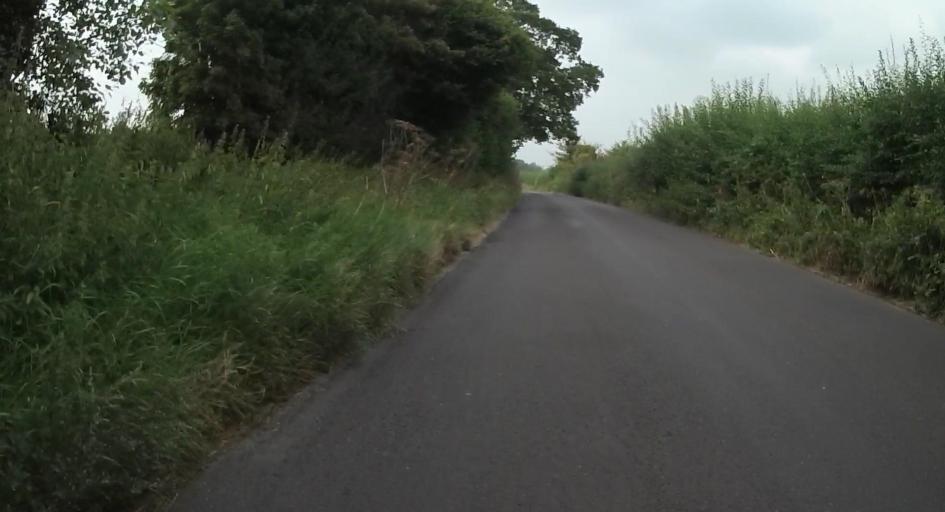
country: GB
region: England
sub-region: Hampshire
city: Old Basing
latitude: 51.2504
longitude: -1.0428
